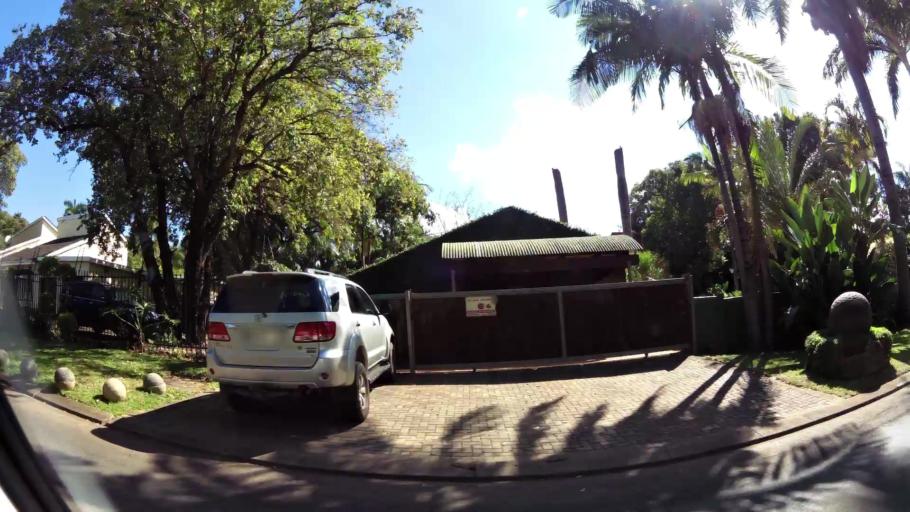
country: ZA
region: Limpopo
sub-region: Mopani District Municipality
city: Tzaneen
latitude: -23.8191
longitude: 30.1500
